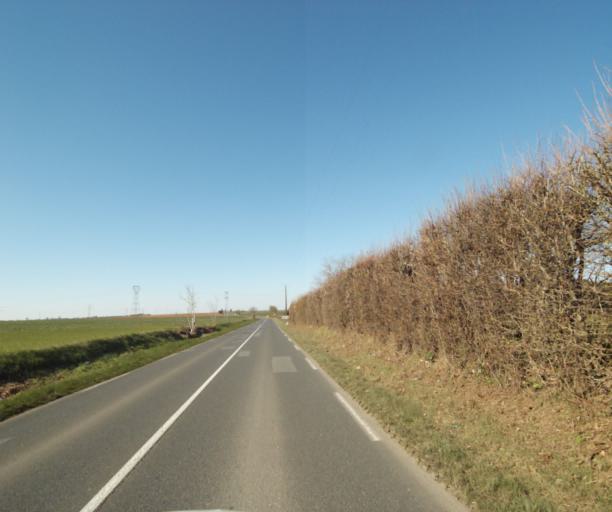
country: FR
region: Poitou-Charentes
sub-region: Departement des Deux-Sevres
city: Saint-Maxire
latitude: 46.3590
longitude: -0.4838
